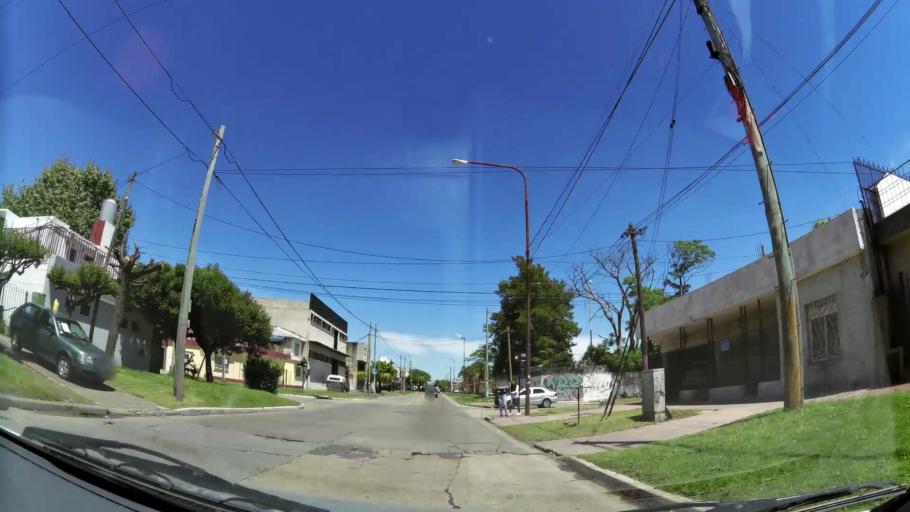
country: AR
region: Buenos Aires
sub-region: Partido de Quilmes
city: Quilmes
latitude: -34.7380
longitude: -58.2903
